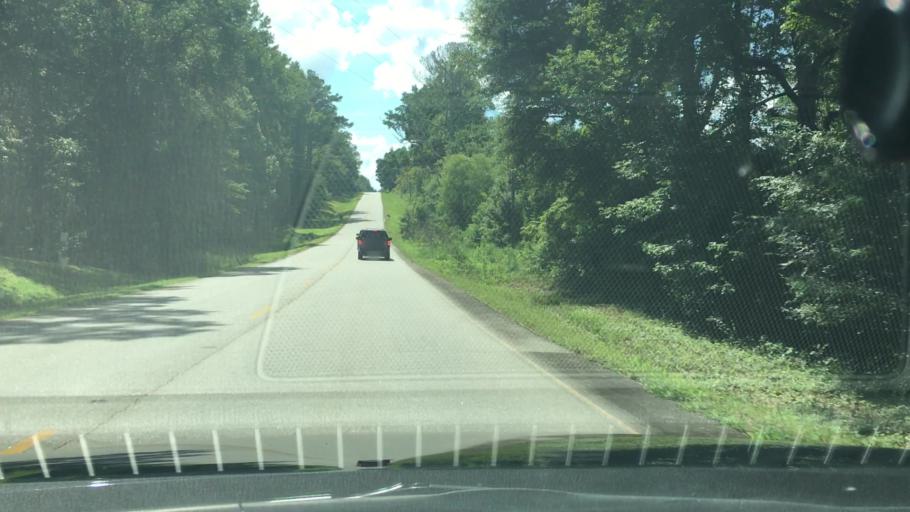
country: US
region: Georgia
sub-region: Jasper County
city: Monticello
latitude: 33.3051
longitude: -83.5887
